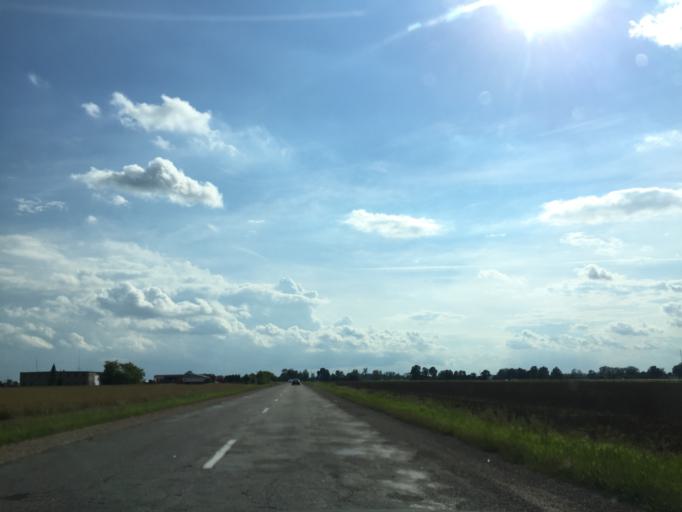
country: LV
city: Tervete
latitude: 56.5634
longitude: 23.4011
